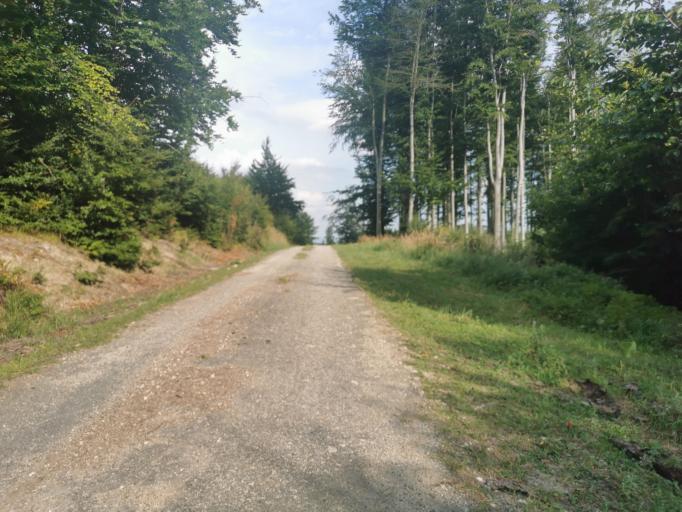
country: SK
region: Nitriansky
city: Stara Tura
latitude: 48.8334
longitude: 17.6298
